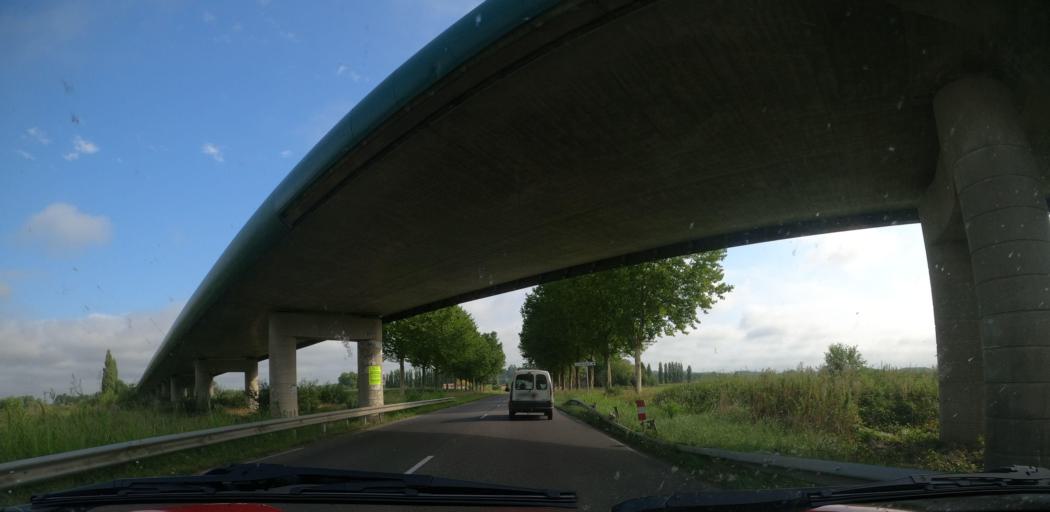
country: FR
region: Aquitaine
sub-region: Departement des Landes
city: Peyrehorade
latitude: 43.5351
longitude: -1.1091
